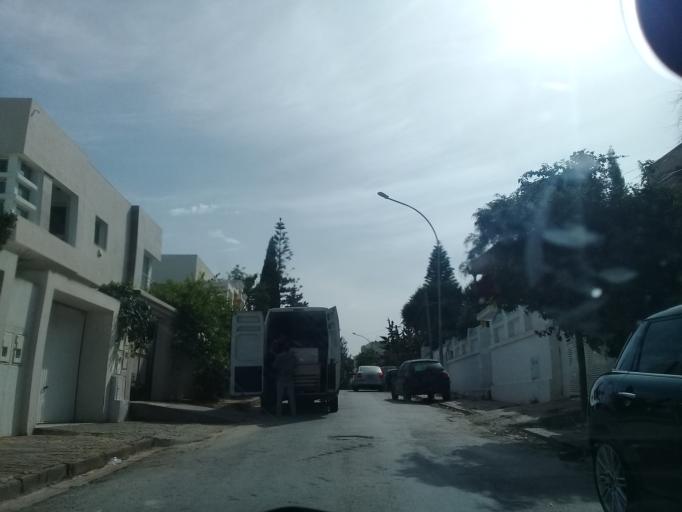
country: TN
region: Tunis
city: Tunis
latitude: 36.8509
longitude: 10.1597
